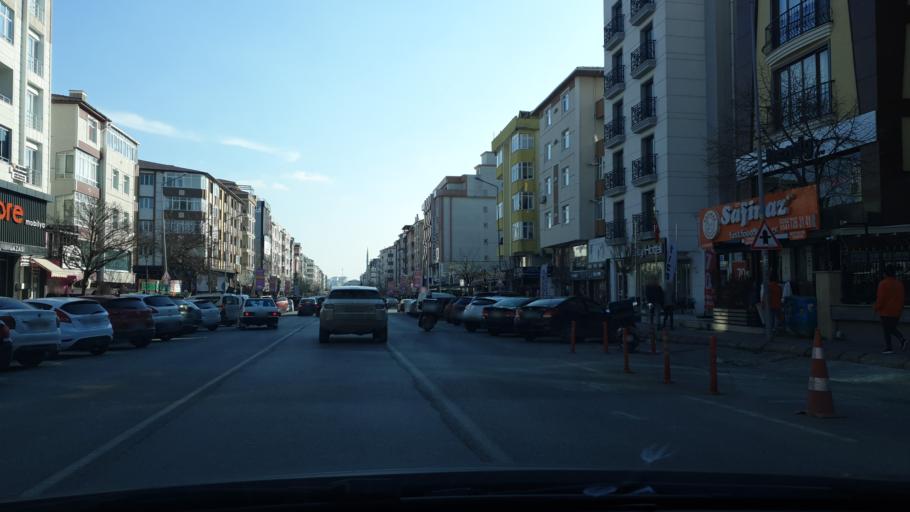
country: TR
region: Tekirdag
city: Cerkezkoey
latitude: 41.2934
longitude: 27.9979
